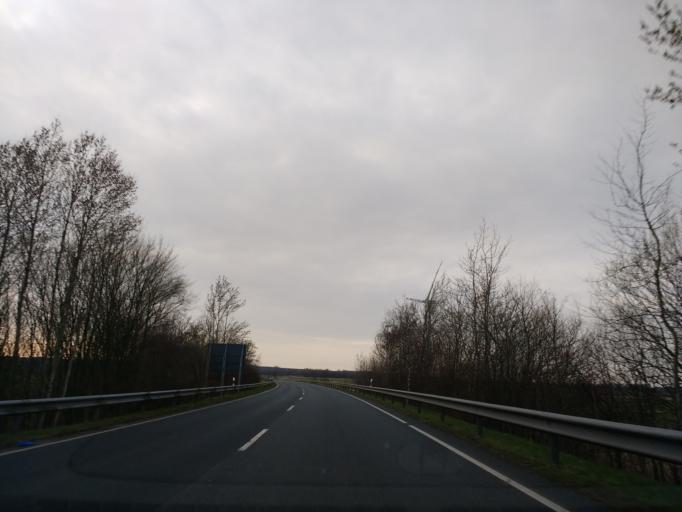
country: DE
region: Lower Saxony
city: Cuxhaven
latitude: 53.8201
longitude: 8.7045
